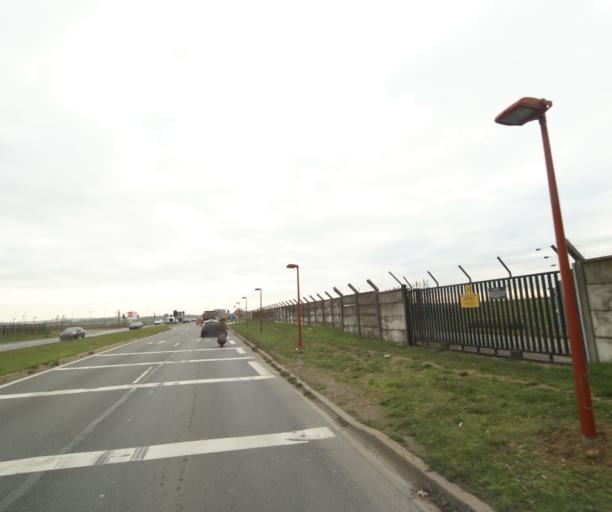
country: FR
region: Ile-de-France
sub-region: Departement du Val-d'Oise
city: Gonesse
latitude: 48.9749
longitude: 2.4597
